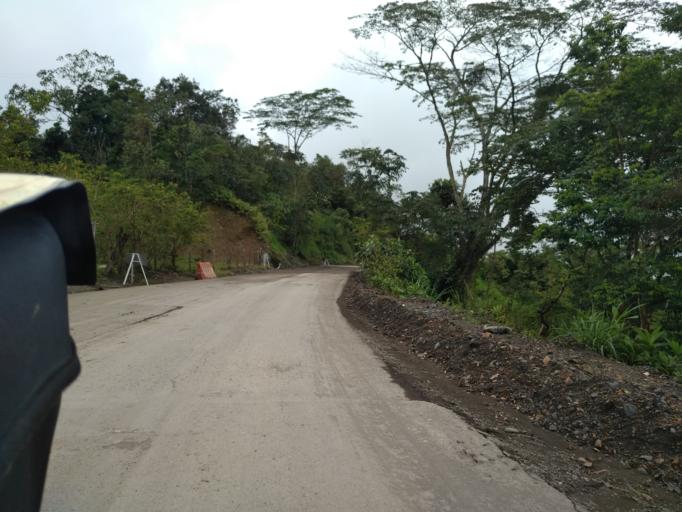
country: CO
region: Santander
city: Landazuri
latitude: 6.1779
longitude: -73.7152
